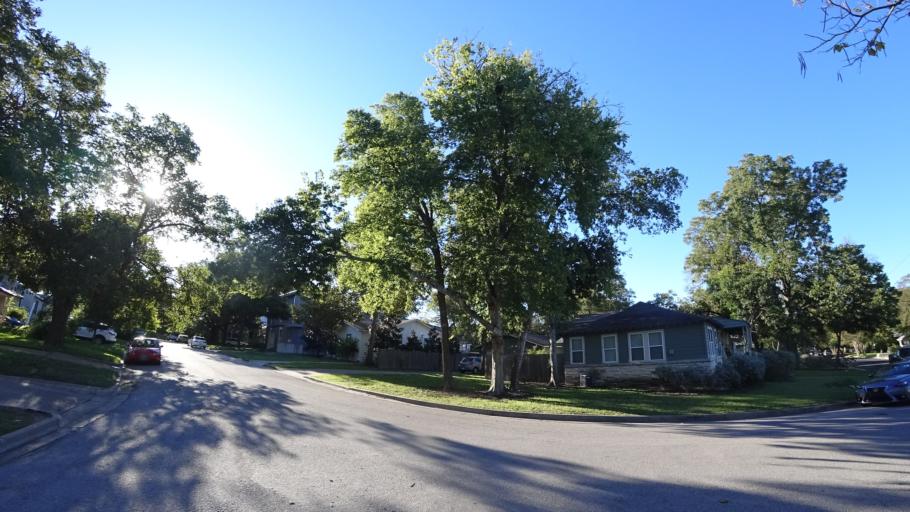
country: US
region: Texas
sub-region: Travis County
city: Austin
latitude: 30.3108
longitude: -97.7208
